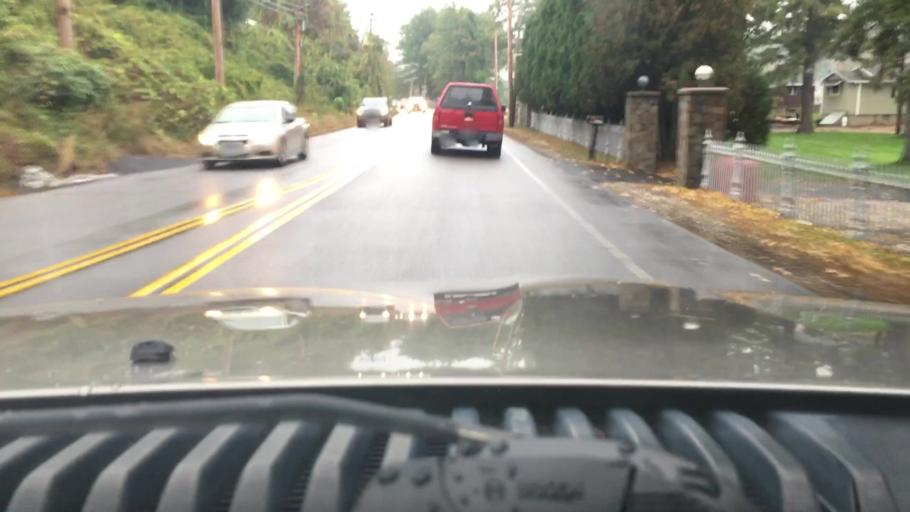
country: US
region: New Hampshire
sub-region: Hillsborough County
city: Manchester
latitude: 43.0196
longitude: -71.4808
